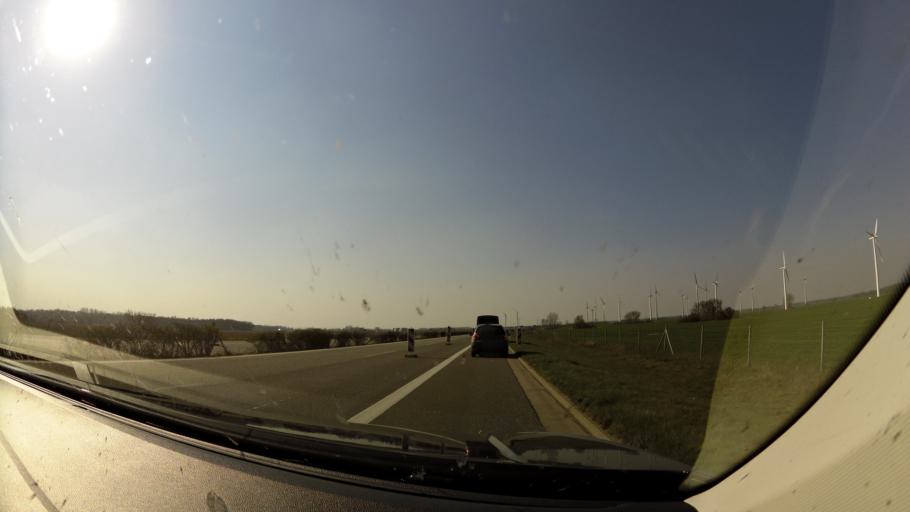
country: DE
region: Mecklenburg-Vorpommern
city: Grimmen
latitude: 54.0815
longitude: 13.0091
